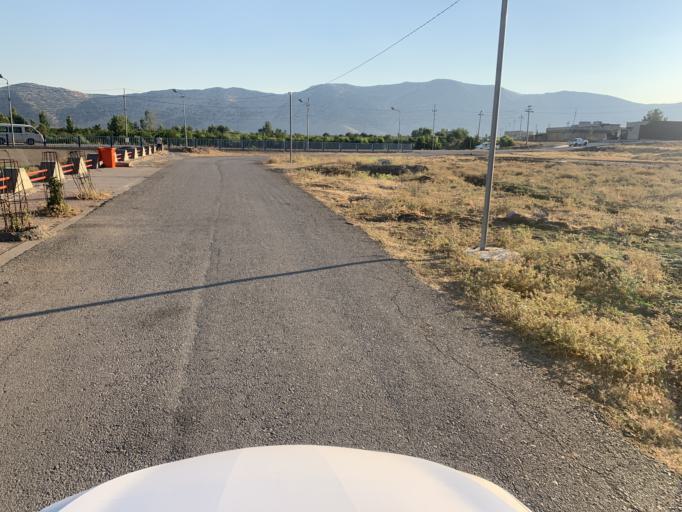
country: IQ
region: As Sulaymaniyah
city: Raniye
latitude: 36.2734
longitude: 44.7510
